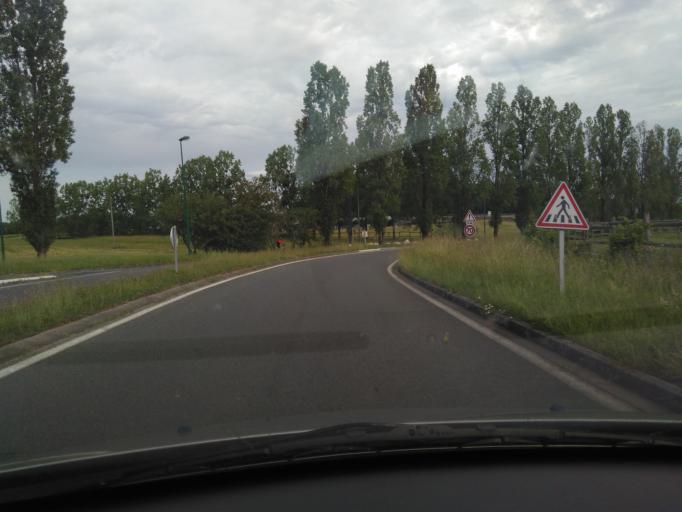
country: FR
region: Centre
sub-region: Departement d'Indre-et-Loire
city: Amboise
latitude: 47.3921
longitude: 0.9799
